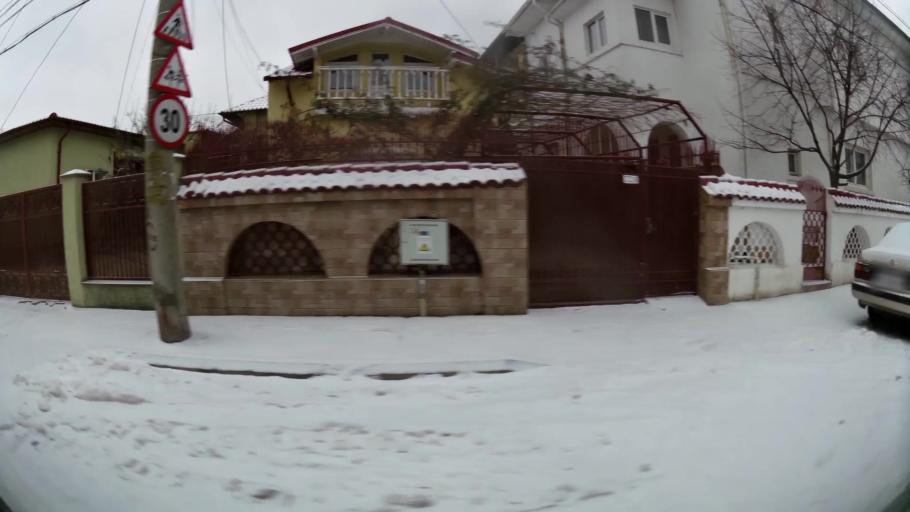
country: RO
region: Prahova
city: Ploiesti
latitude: 44.9384
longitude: 26.0377
